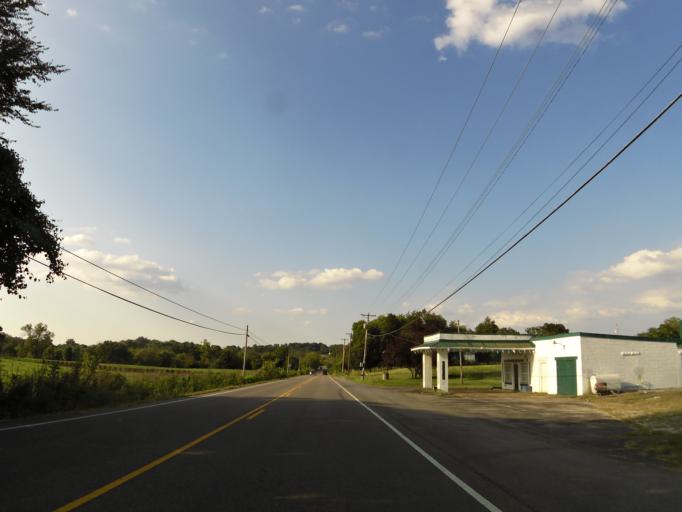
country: US
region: Tennessee
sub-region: Blount County
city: Eagleton Village
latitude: 35.8405
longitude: -83.9413
